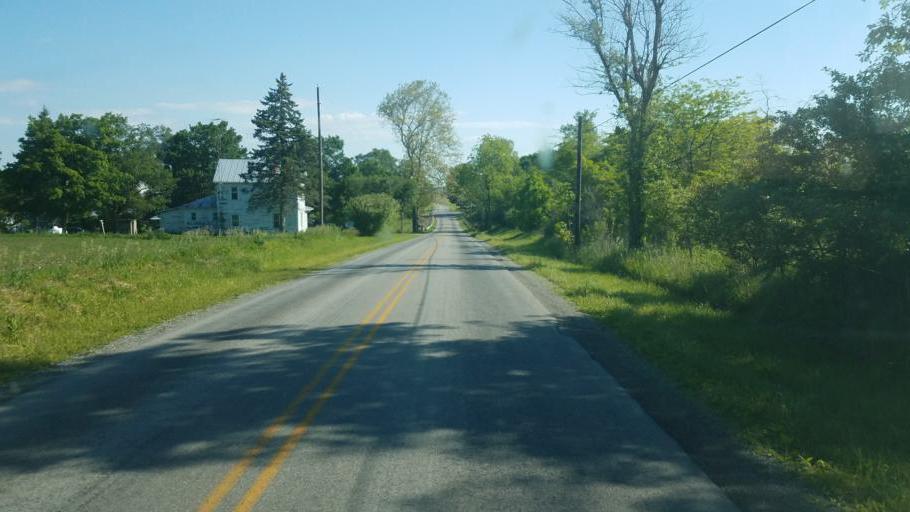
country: US
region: Ohio
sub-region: Hardin County
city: Kenton
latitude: 40.5919
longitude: -83.6181
